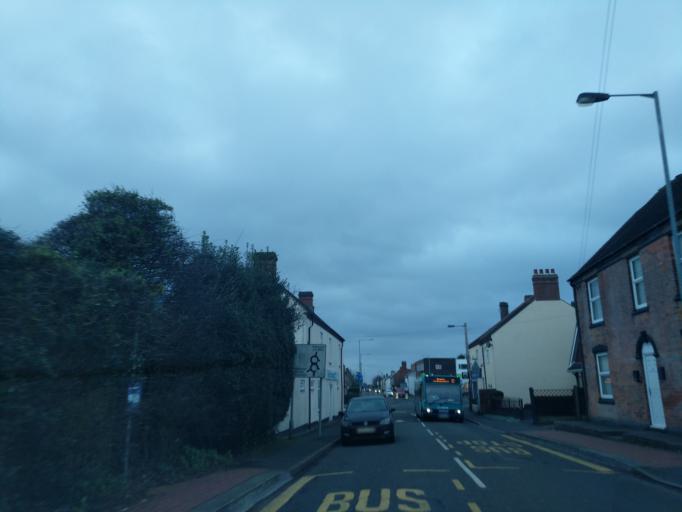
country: GB
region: England
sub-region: Staffordshire
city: Cannock
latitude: 52.7004
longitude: -2.0207
